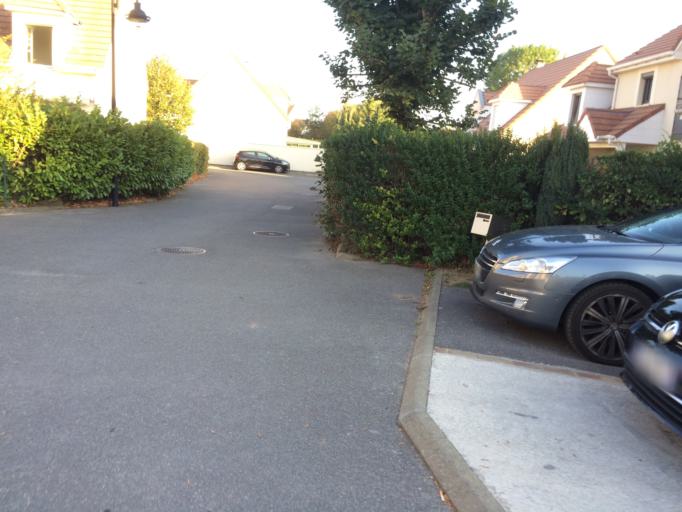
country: FR
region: Ile-de-France
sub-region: Departement de l'Essonne
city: Nozay
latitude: 48.6573
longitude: 2.2400
